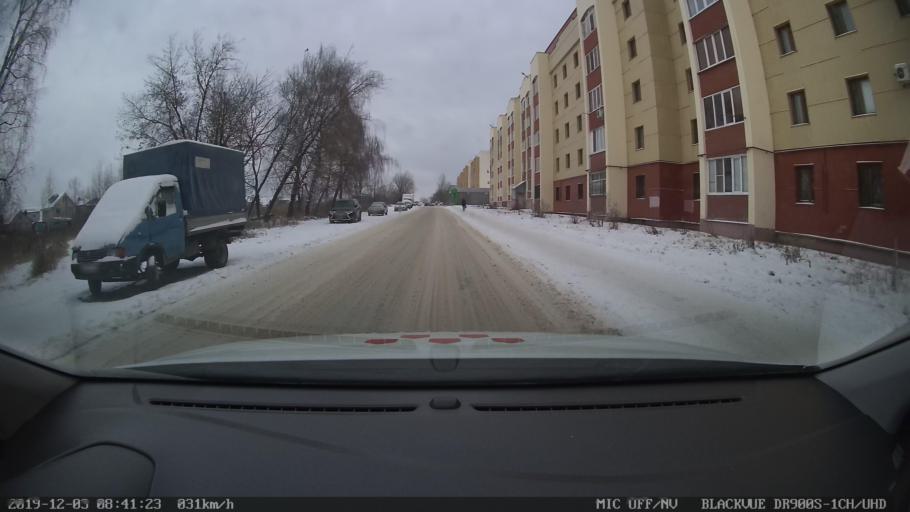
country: RU
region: Tatarstan
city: Staroye Arakchino
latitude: 55.8766
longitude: 49.0207
